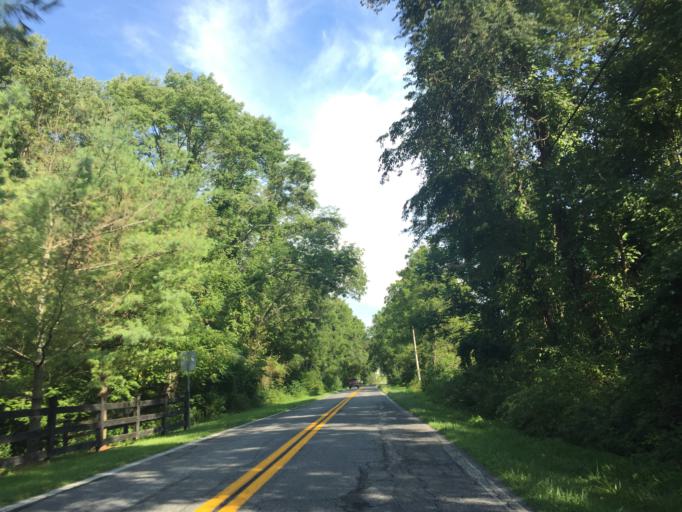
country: US
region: Maryland
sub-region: Carroll County
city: Manchester
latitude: 39.6285
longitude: -76.8944
